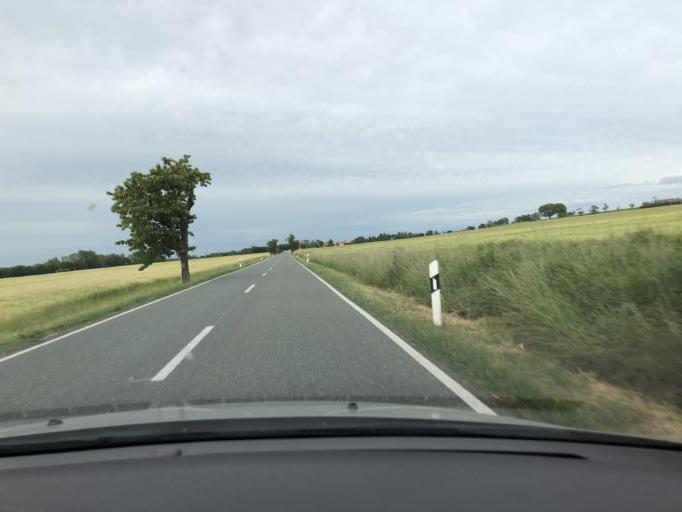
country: DE
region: Thuringia
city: Kleinobringen
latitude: 51.0333
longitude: 11.3172
